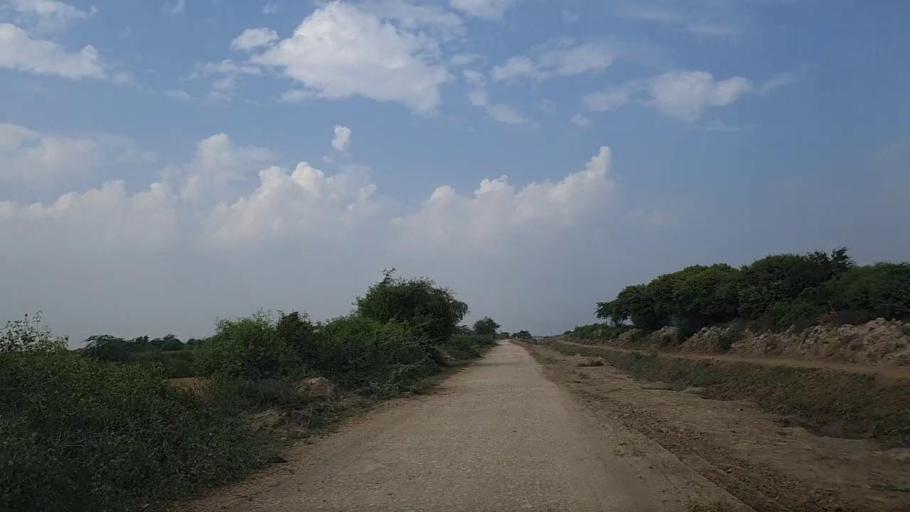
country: PK
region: Sindh
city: Daro Mehar
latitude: 24.7172
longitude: 68.1398
